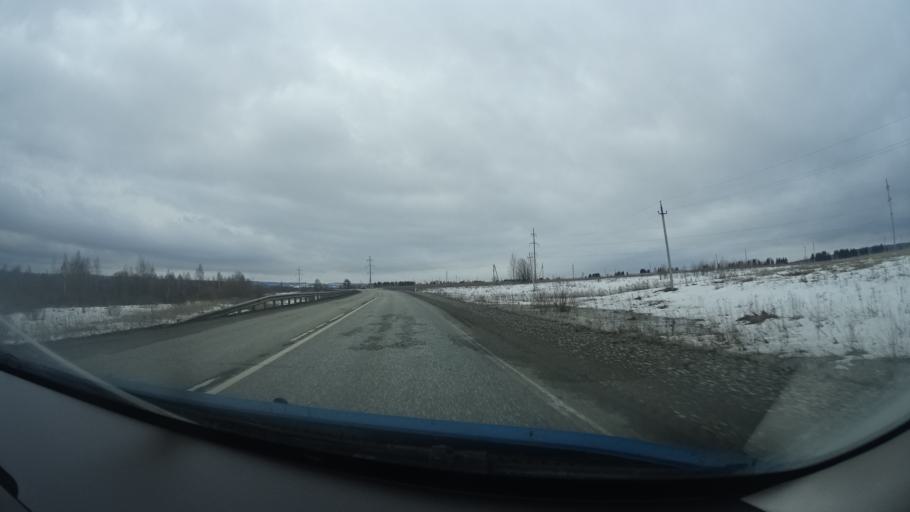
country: RU
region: Perm
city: Barda
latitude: 56.9510
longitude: 55.5837
